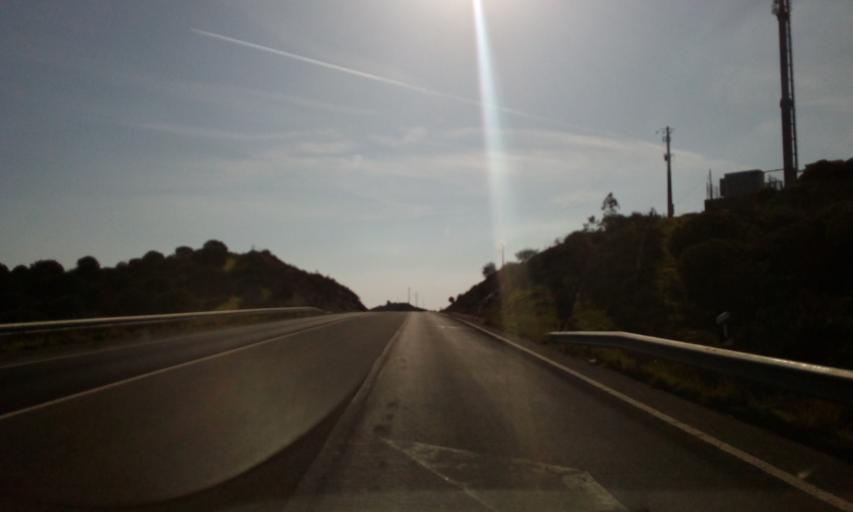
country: PT
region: Faro
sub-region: Castro Marim
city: Castro Marim
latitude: 37.2661
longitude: -7.4951
